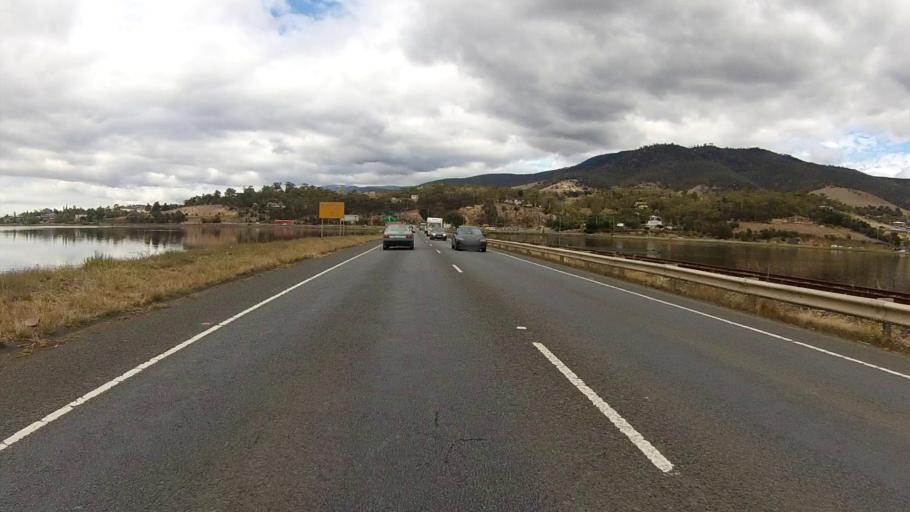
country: AU
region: Tasmania
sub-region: Glenorchy
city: Granton
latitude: -42.7456
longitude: 147.2249
